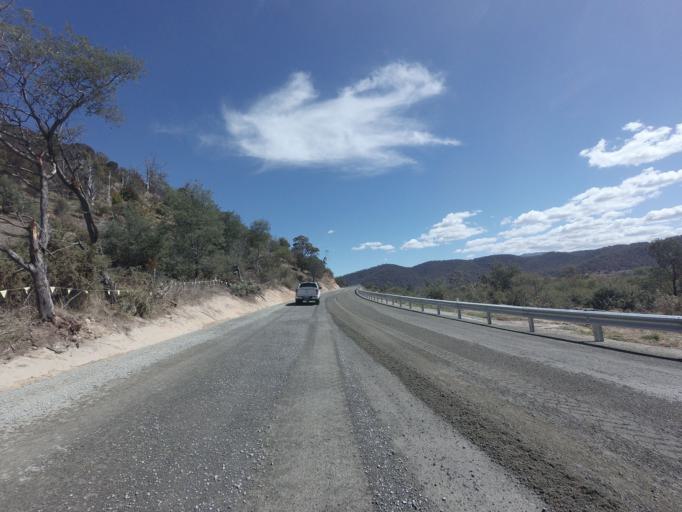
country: AU
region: Tasmania
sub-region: Break O'Day
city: St Helens
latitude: -41.6564
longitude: 147.9207
